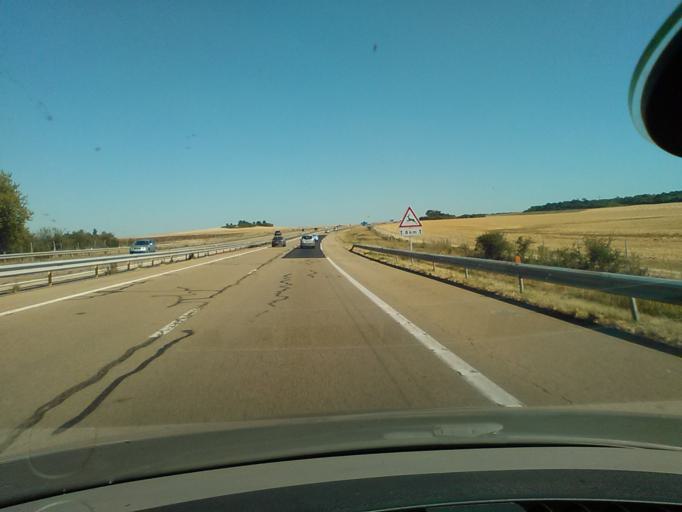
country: FR
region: Bourgogne
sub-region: Departement de l'Yonne
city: Joux-la-Ville
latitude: 47.6578
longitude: 3.8912
